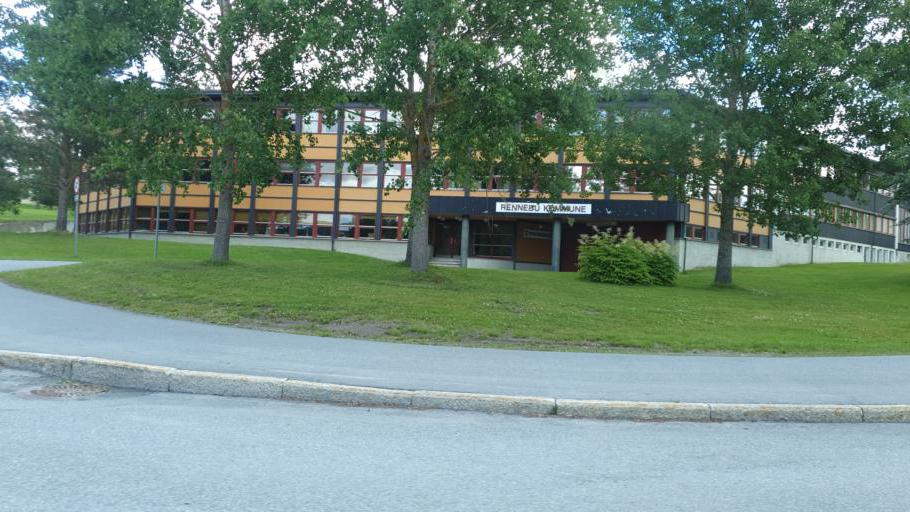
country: NO
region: Sor-Trondelag
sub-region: Rennebu
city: Berkak
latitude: 62.8284
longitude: 10.0044
